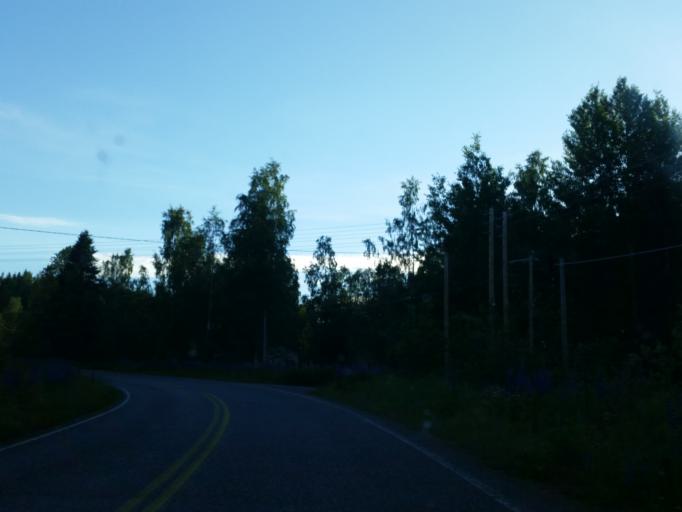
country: FI
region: Northern Savo
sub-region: Sisae-Savo
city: Tervo
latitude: 63.0296
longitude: 26.6972
